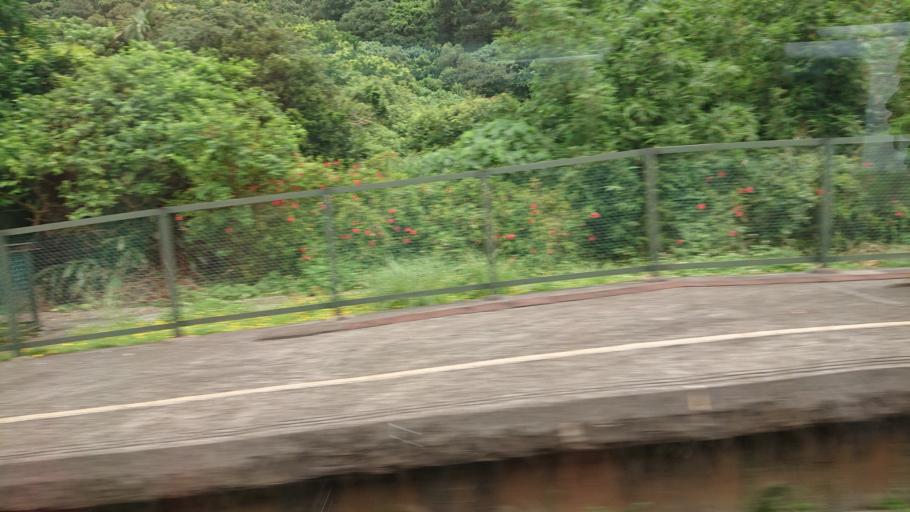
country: TW
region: Taiwan
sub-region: Yilan
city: Yilan
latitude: 24.9375
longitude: 121.8884
